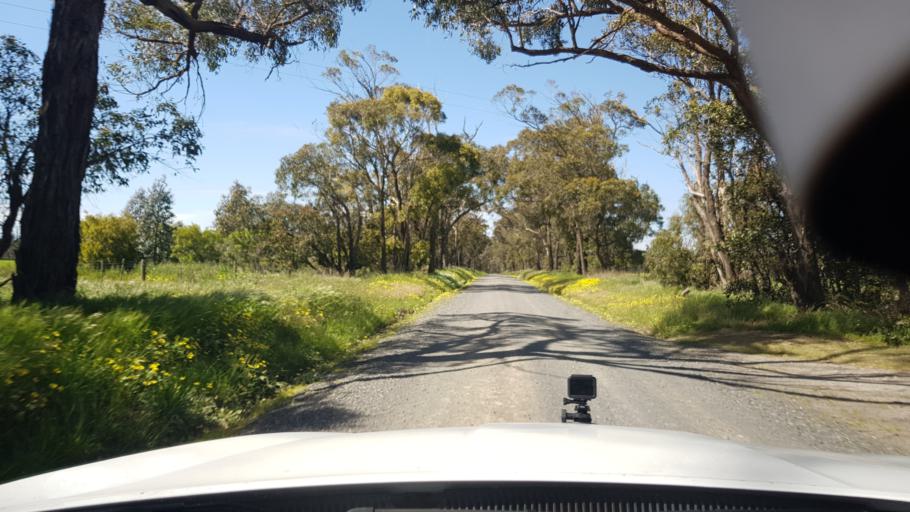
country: AU
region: Victoria
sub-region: Latrobe
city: Moe
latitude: -38.1427
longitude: 146.1167
